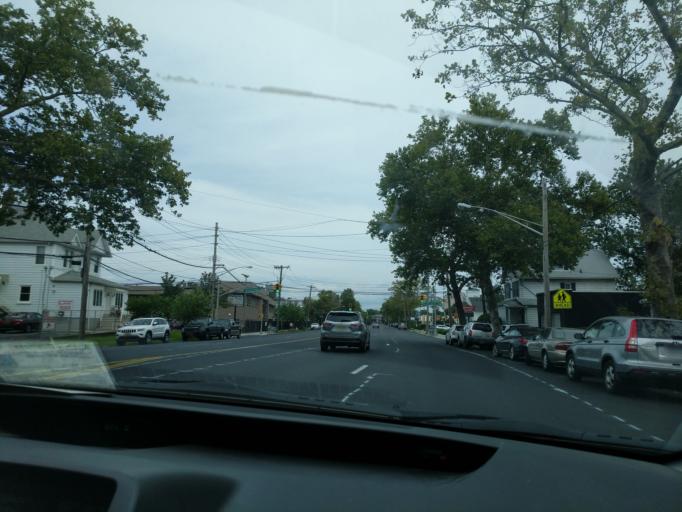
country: US
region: New York
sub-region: Richmond County
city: Bloomfield
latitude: 40.6092
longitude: -74.1607
